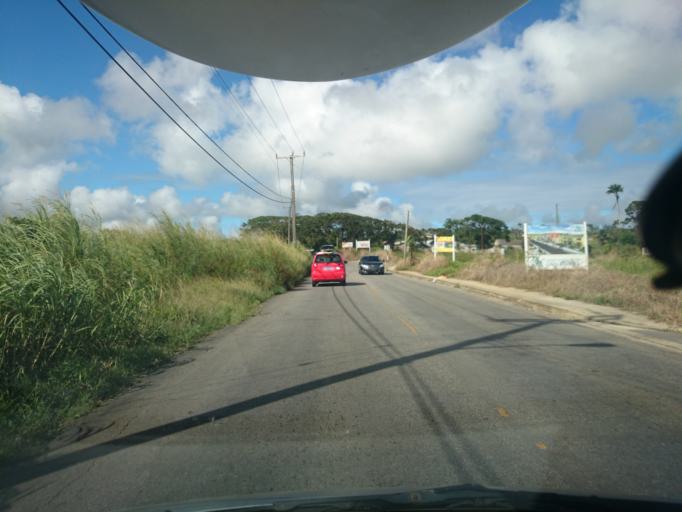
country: BB
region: Saint Thomas
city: Welchman Hall
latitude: 13.1500
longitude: -59.5530
